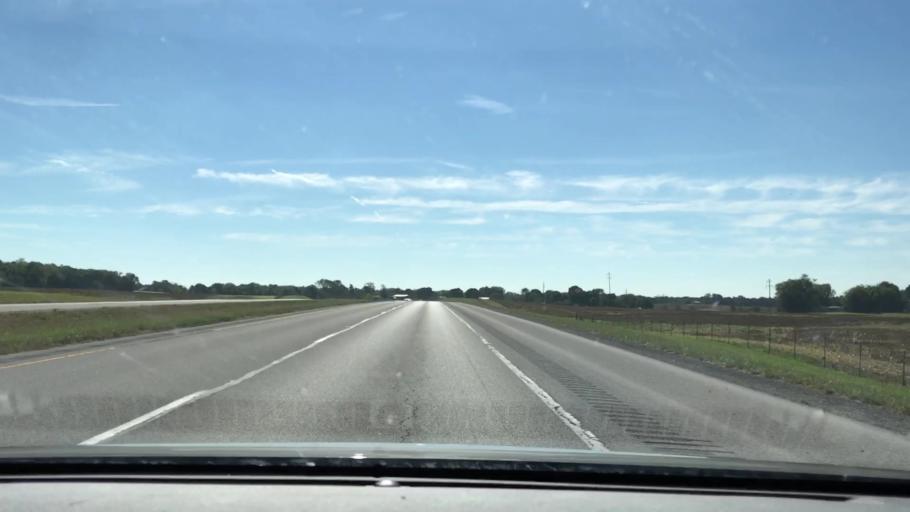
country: US
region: Kentucky
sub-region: Todd County
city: Elkton
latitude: 36.8154
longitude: -87.1410
